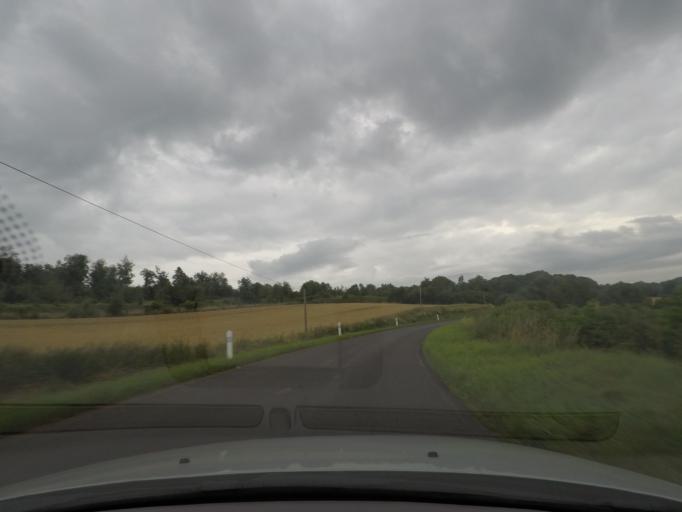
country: FR
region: Haute-Normandie
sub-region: Departement de la Seine-Maritime
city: Neufchatel-en-Bray
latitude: 49.7318
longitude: 1.4651
